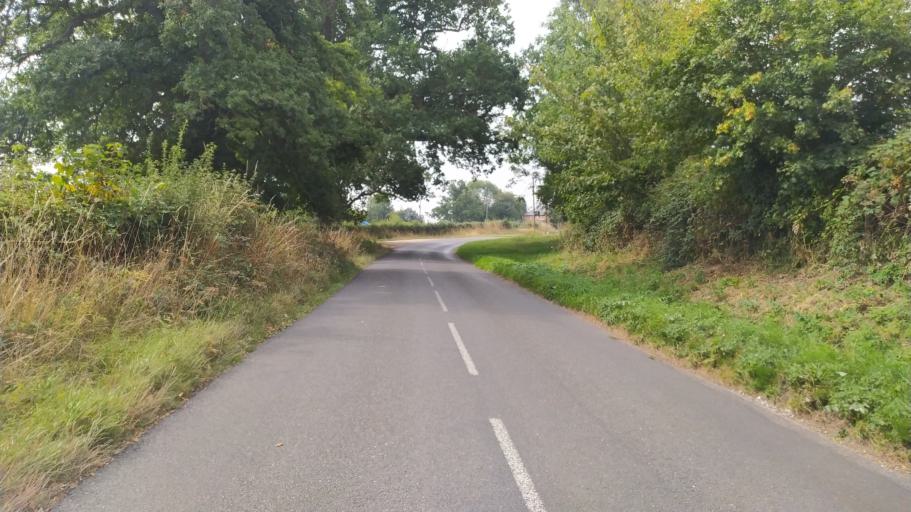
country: GB
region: England
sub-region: Hampshire
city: Chandlers Ford
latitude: 51.0046
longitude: -1.4337
